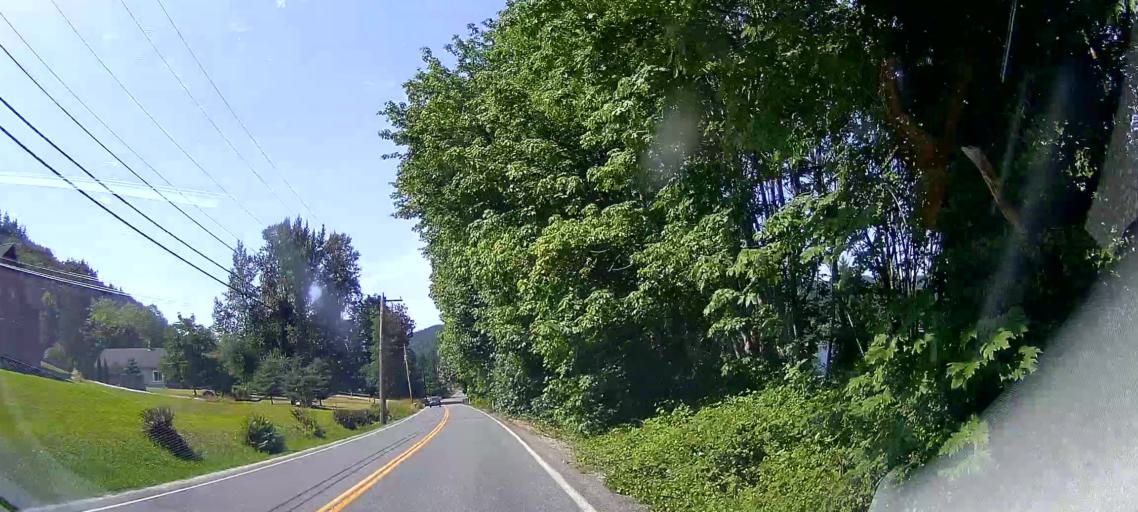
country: US
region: Washington
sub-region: Skagit County
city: Big Lake
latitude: 48.3119
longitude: -122.2293
